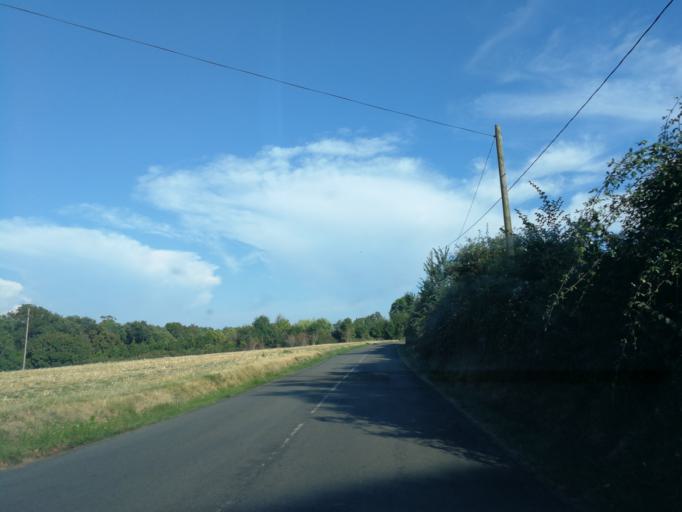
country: FR
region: Midi-Pyrenees
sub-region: Departement de la Haute-Garonne
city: Balma
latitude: 43.6161
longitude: 1.5230
